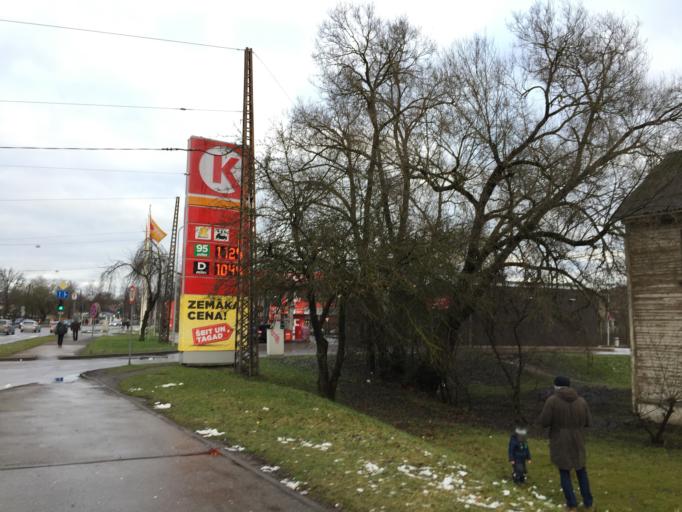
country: LV
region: Marupe
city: Marupe
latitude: 56.9580
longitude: 24.0522
